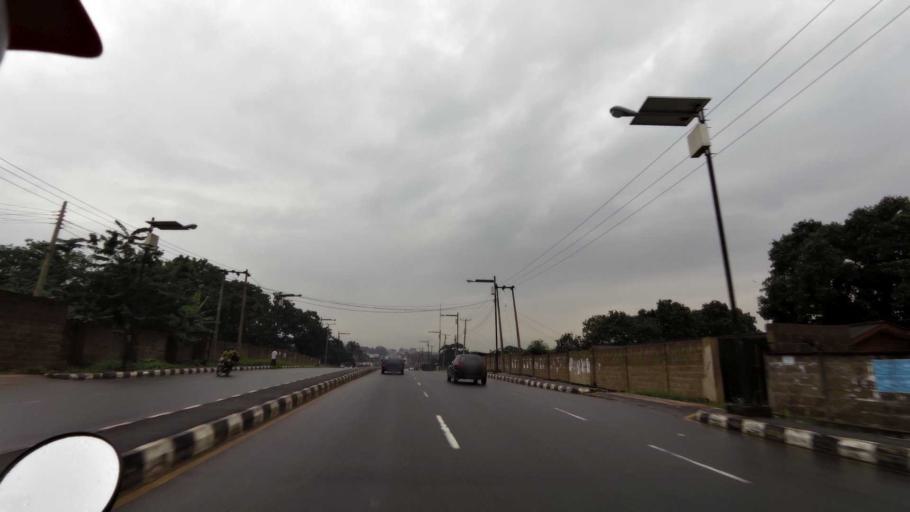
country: NG
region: Oyo
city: Ibadan
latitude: 7.3988
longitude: 3.9058
